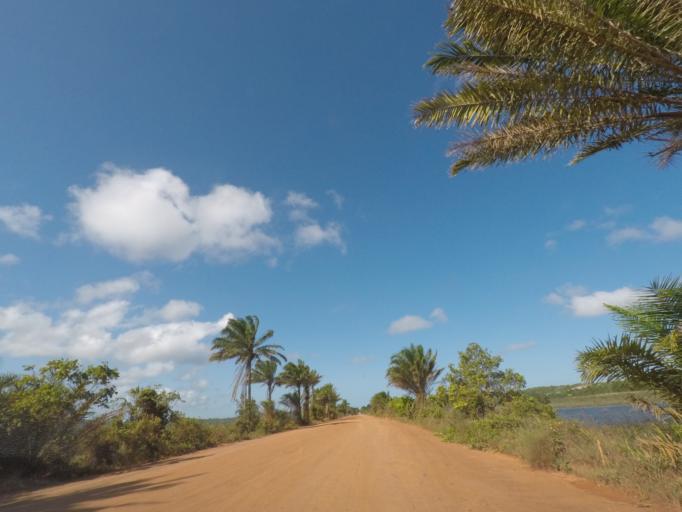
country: BR
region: Bahia
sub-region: Marau
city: Marau
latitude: -14.1485
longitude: -39.0049
